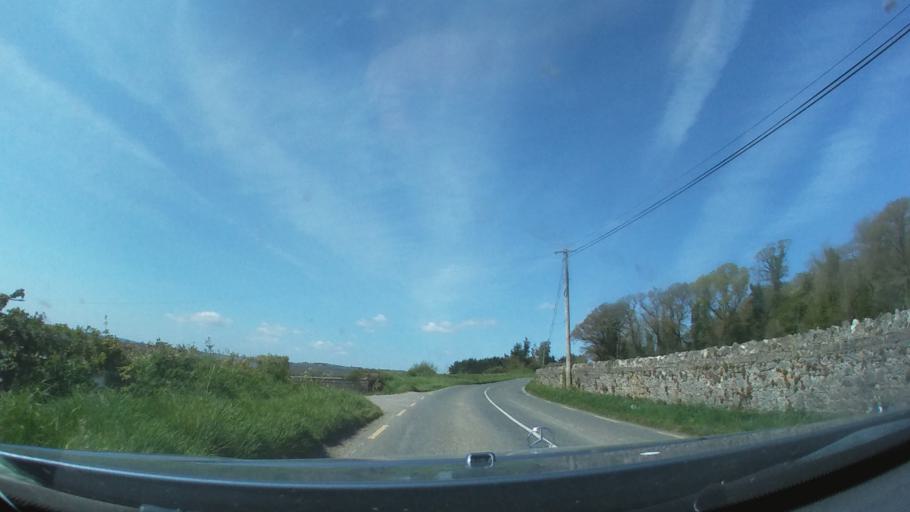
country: IE
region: Leinster
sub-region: Kilkenny
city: Callan
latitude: 52.6071
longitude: -7.3963
